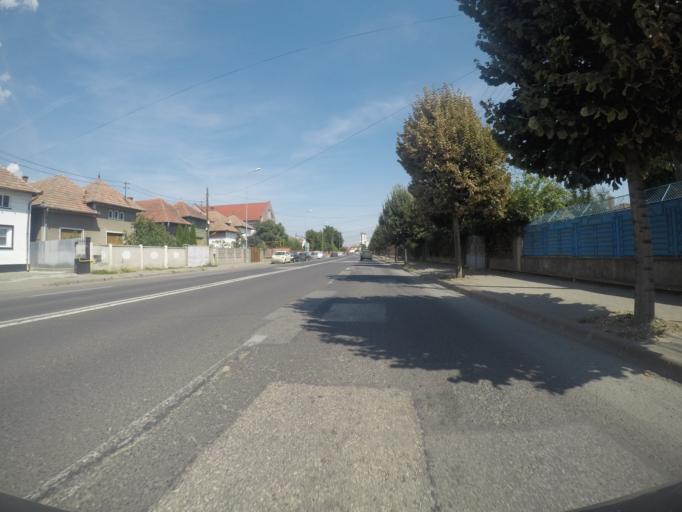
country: RO
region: Alba
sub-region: Municipiul Alba Iulia
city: Alba Iulia
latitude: 46.0726
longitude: 23.5669
